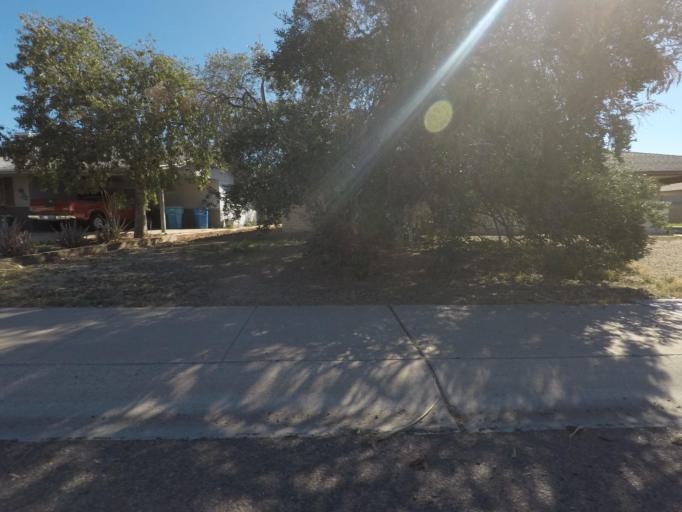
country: US
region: Arizona
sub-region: Maricopa County
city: Glendale
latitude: 33.5396
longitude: -112.1217
